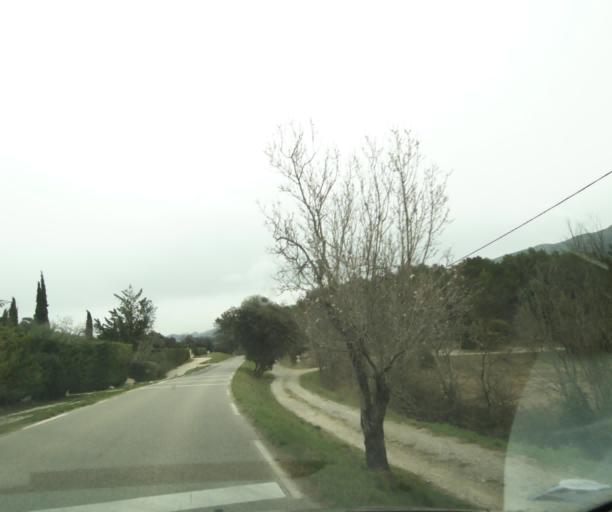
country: FR
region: Provence-Alpes-Cote d'Azur
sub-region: Departement des Bouches-du-Rhone
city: Saint-Marc-Jaumegarde
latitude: 43.5551
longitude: 5.5757
